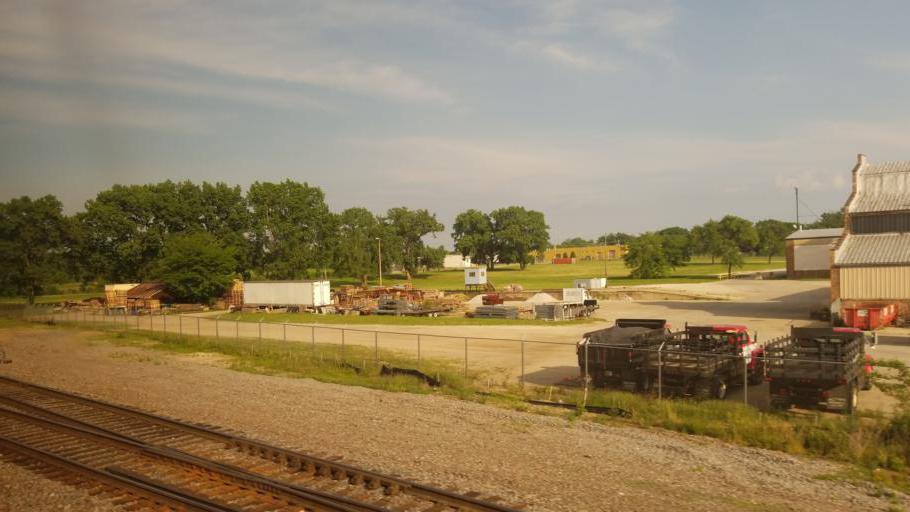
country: US
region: Illinois
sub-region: Kane County
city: Aurora
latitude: 41.7698
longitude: -88.2773
